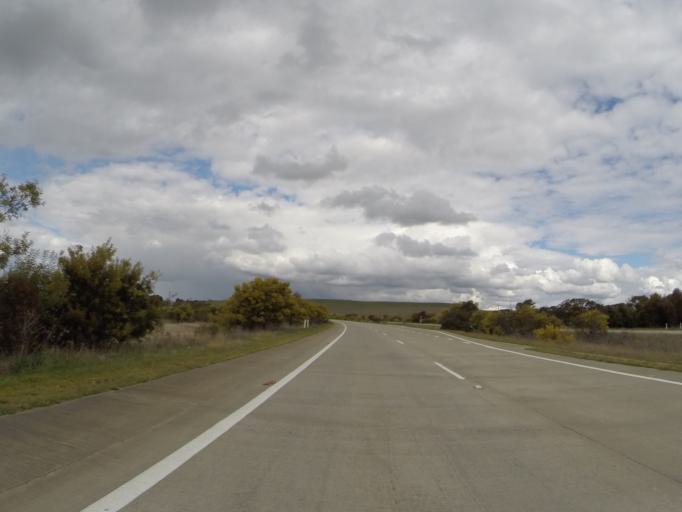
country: AU
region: New South Wales
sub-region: Goulburn Mulwaree
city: Goulburn
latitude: -34.8060
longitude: 149.5156
